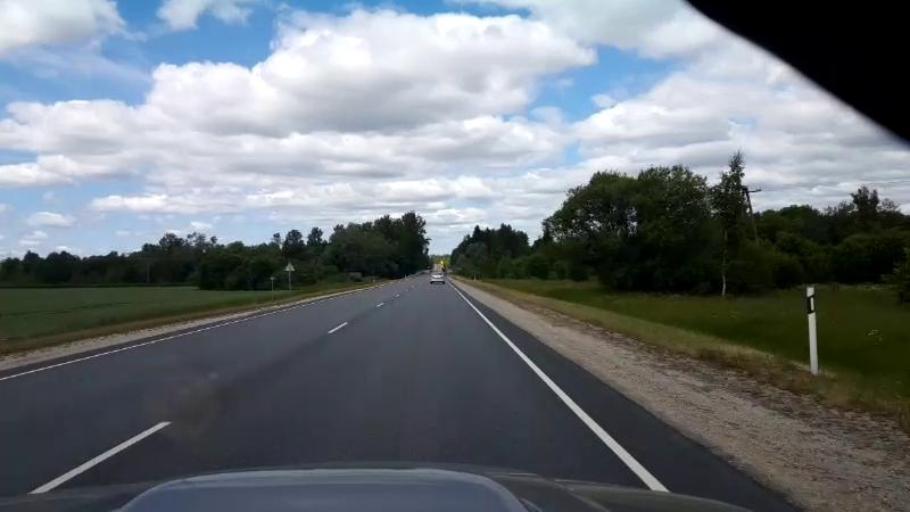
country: EE
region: Paernumaa
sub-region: Halinga vald
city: Parnu-Jaagupi
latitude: 58.6989
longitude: 24.4289
